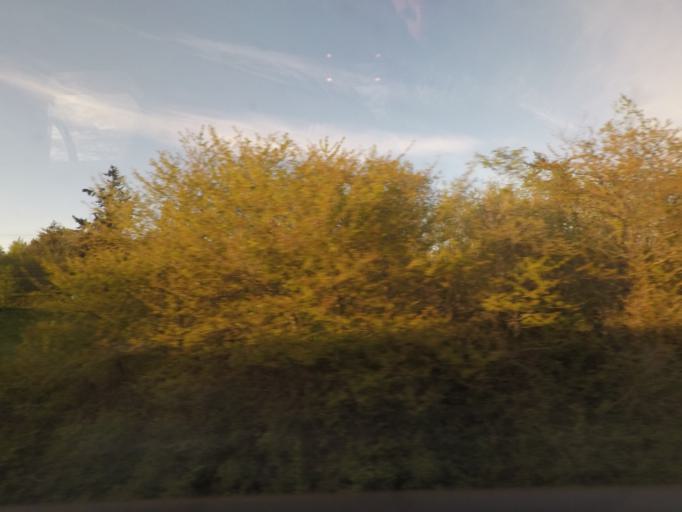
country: US
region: Washington
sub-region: Whatcom County
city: Marietta-Alderwood
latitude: 48.7792
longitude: -122.5406
